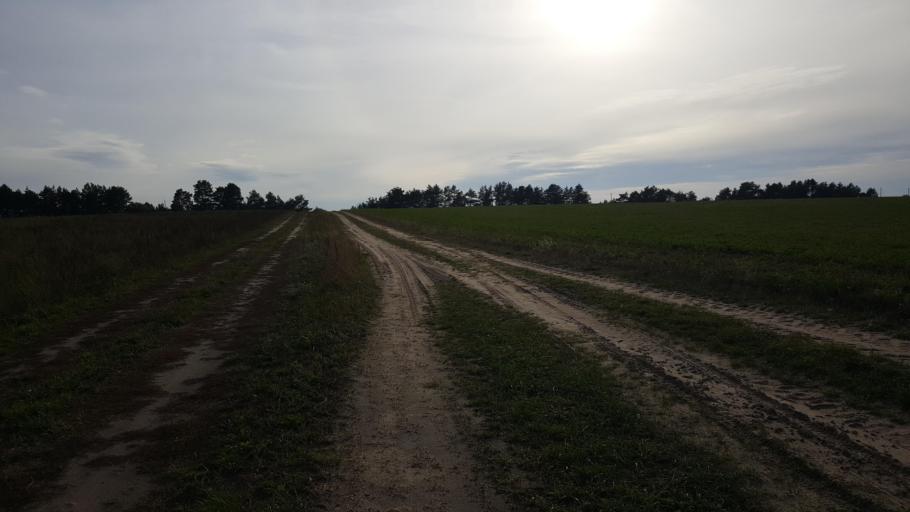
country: BY
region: Brest
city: Kamyanyets
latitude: 52.4005
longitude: 23.8570
